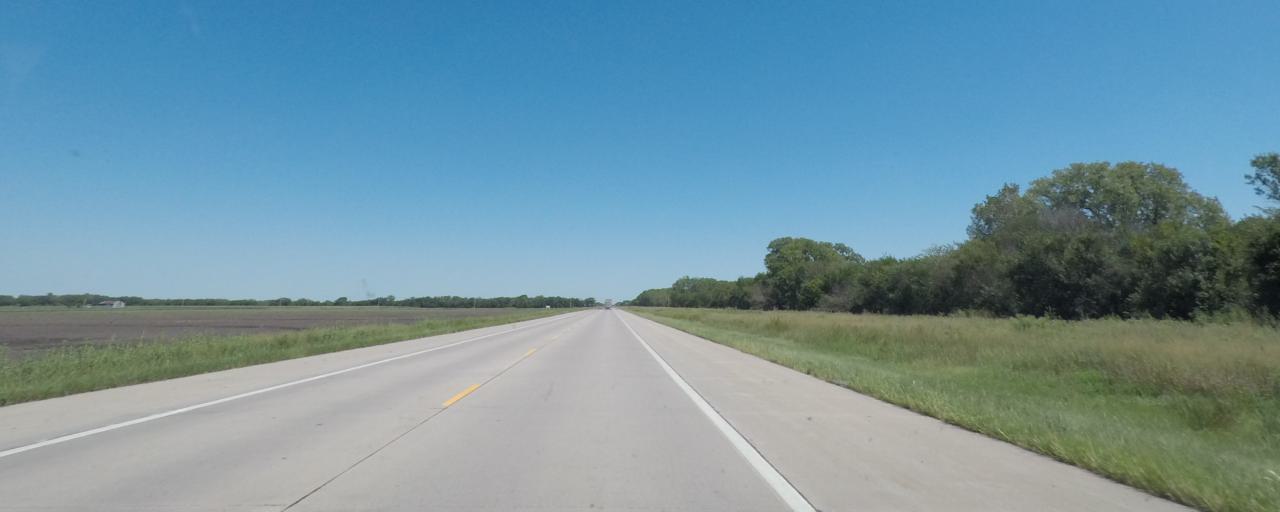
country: US
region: Kansas
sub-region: Chase County
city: Cottonwood Falls
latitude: 38.4069
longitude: -96.3801
